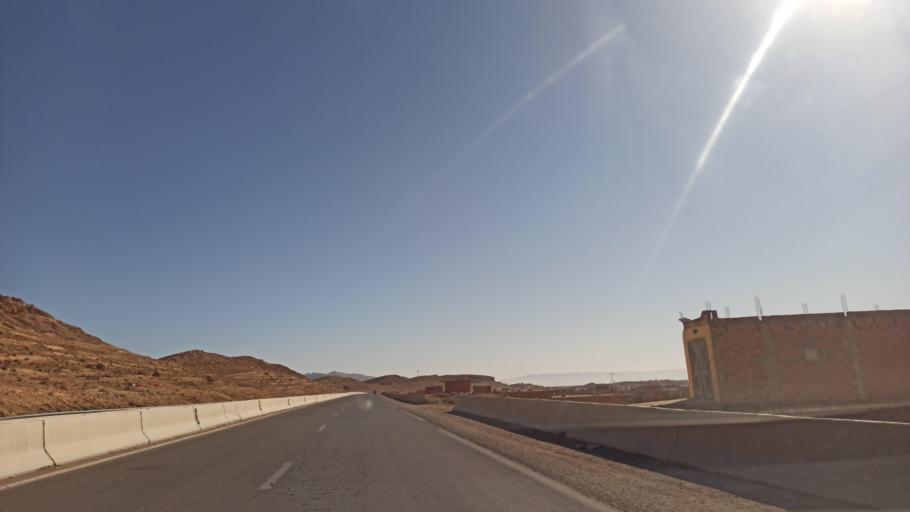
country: TN
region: Gafsa
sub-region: Gafsa Municipality
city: Gafsa
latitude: 34.4506
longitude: 8.7809
